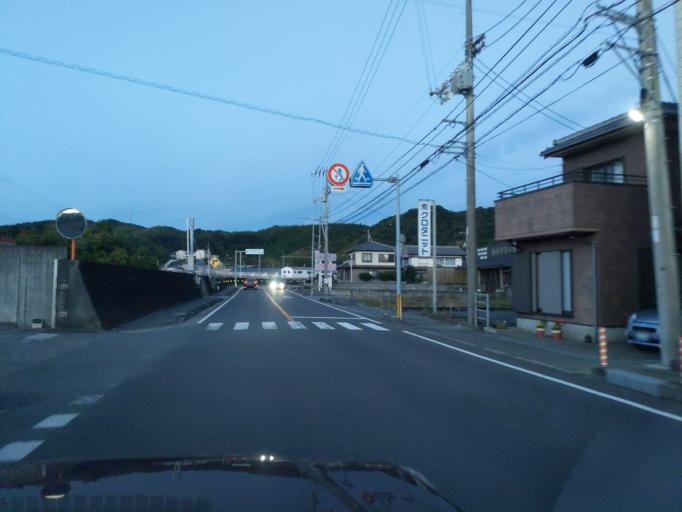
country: JP
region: Tokushima
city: Anan
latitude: 33.8722
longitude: 134.6396
